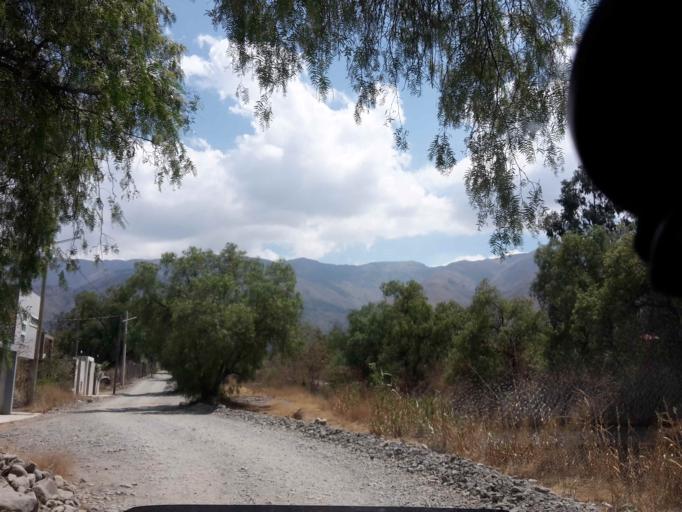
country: BO
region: Cochabamba
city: Cochabamba
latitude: -17.3440
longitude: -66.2124
